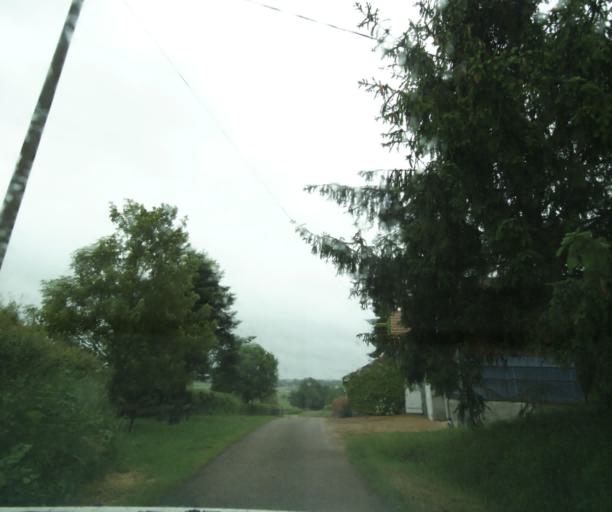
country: FR
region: Bourgogne
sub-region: Departement de Saone-et-Loire
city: Palinges
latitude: 46.4940
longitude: 4.1942
